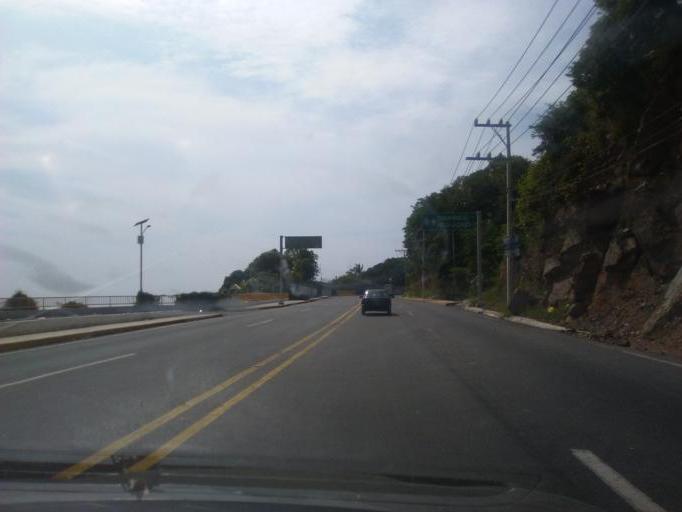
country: MX
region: Guerrero
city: Acapulco de Juarez
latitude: 16.8803
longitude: -99.9450
